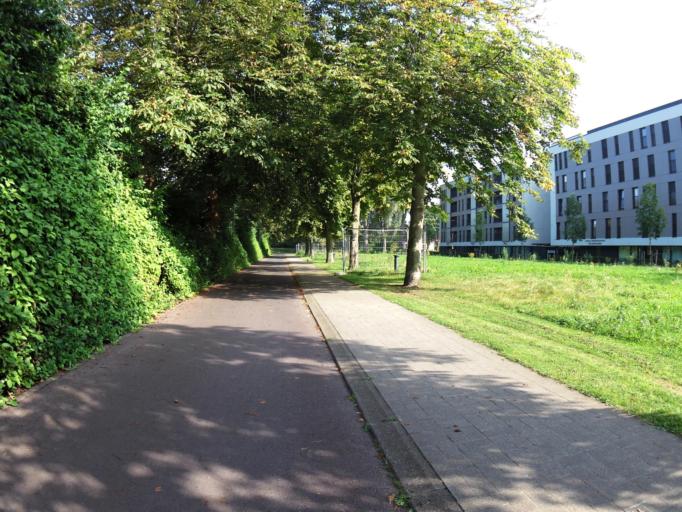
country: BE
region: Flanders
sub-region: Provincie West-Vlaanderen
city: Brugge
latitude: 51.1857
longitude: 3.2133
